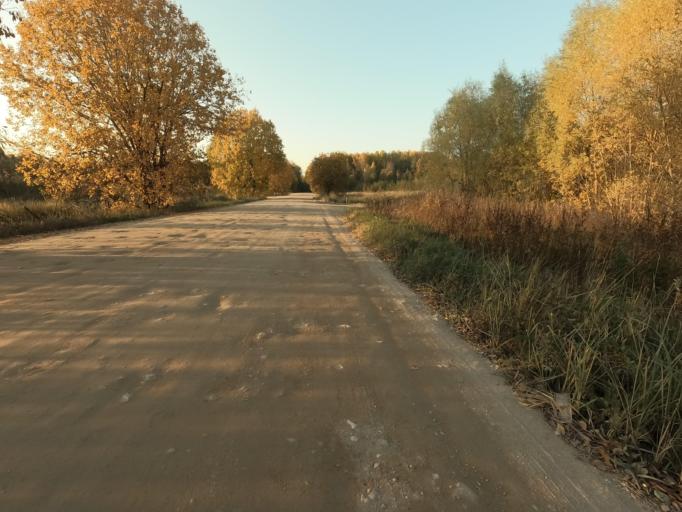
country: RU
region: Leningrad
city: Lyuban'
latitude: 59.0102
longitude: 31.0907
